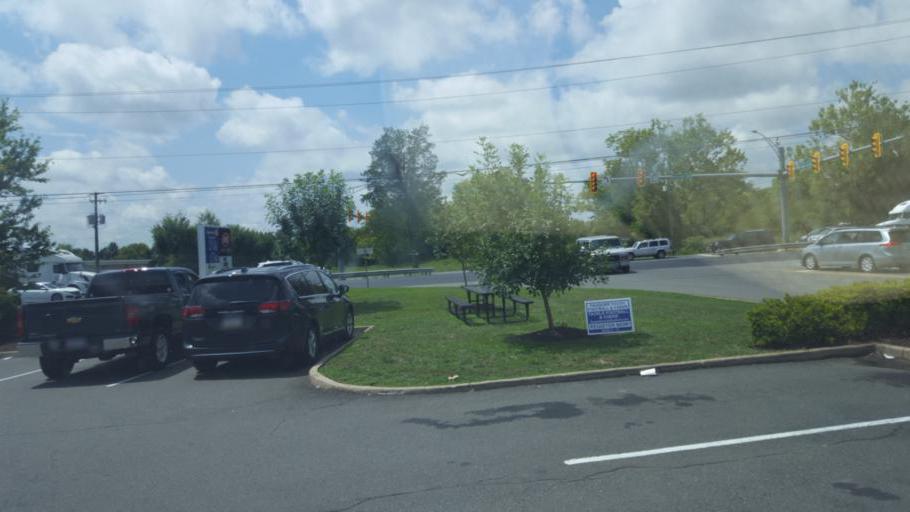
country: US
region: Virginia
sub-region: Fauquier County
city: Bealeton
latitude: 38.5803
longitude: -77.7664
